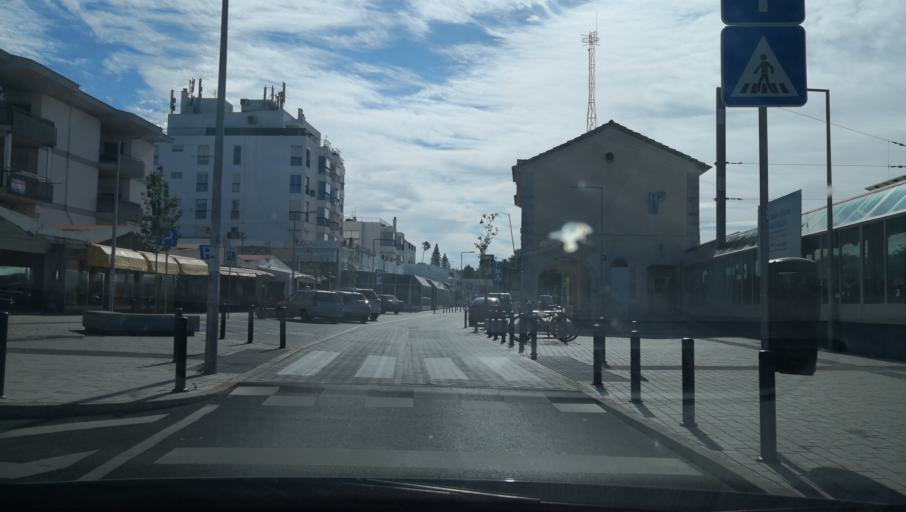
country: PT
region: Lisbon
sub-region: Oeiras
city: Carcavelos
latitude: 38.6879
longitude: -9.3378
